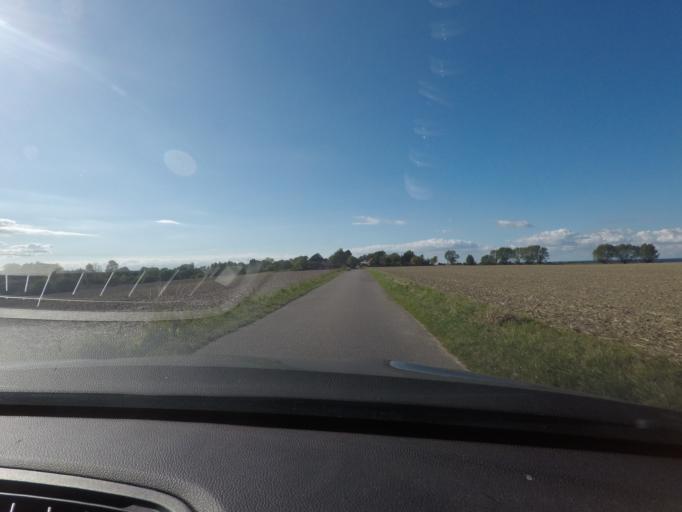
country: DK
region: Zealand
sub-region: Guldborgsund Kommune
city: Sakskobing
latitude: 54.9785
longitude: 11.5420
